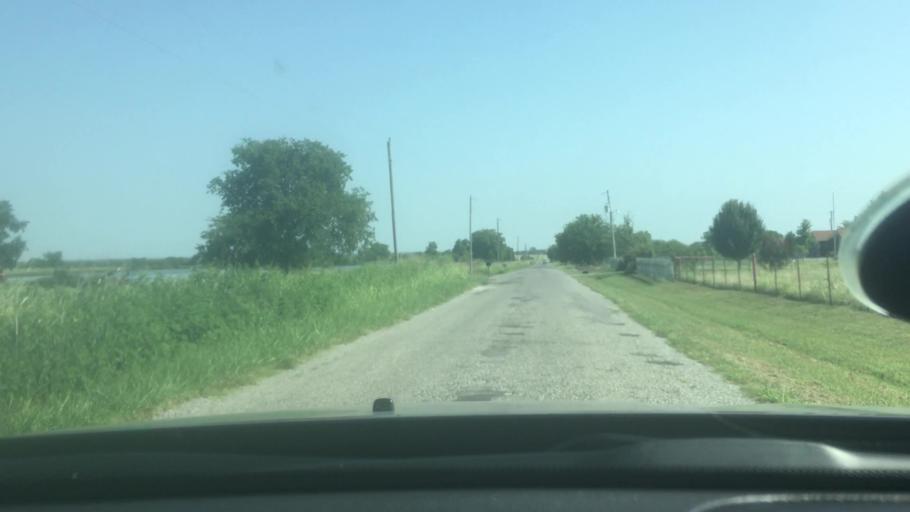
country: US
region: Oklahoma
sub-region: Bryan County
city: Calera
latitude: 33.9650
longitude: -96.4656
